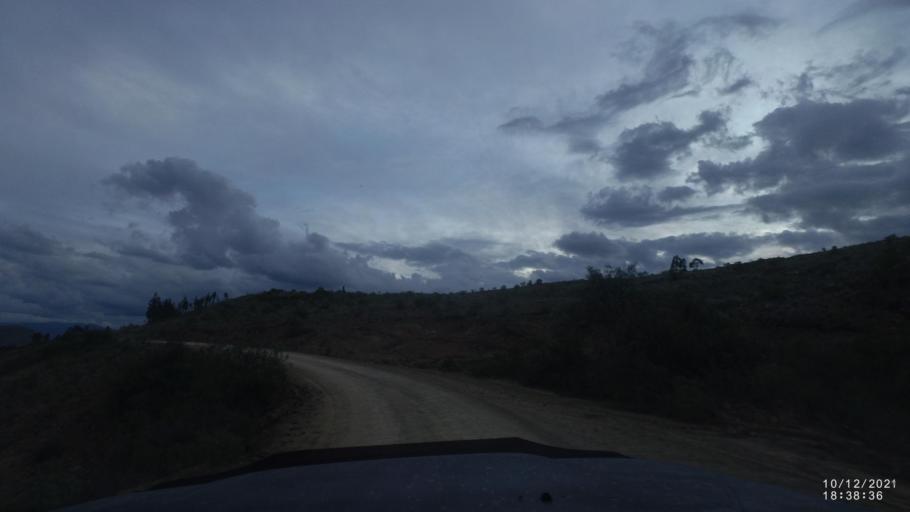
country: BO
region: Cochabamba
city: Tarata
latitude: -17.8433
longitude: -65.9897
